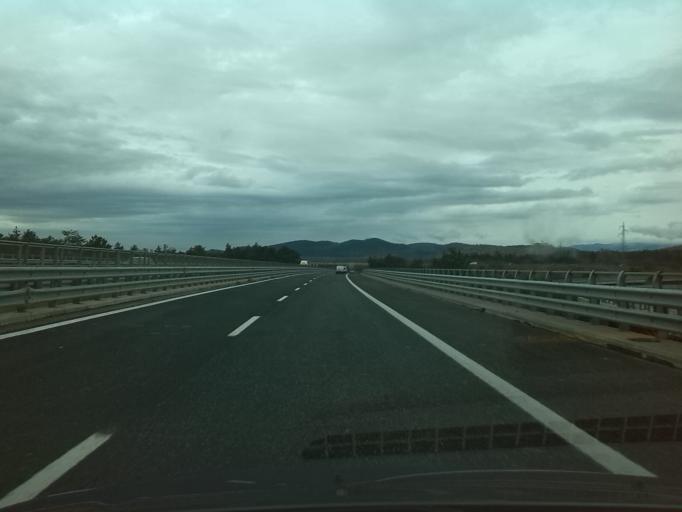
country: IT
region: Friuli Venezia Giulia
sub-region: Provincia di Trieste
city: Villa Opicina
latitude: 45.6893
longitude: 13.8096
